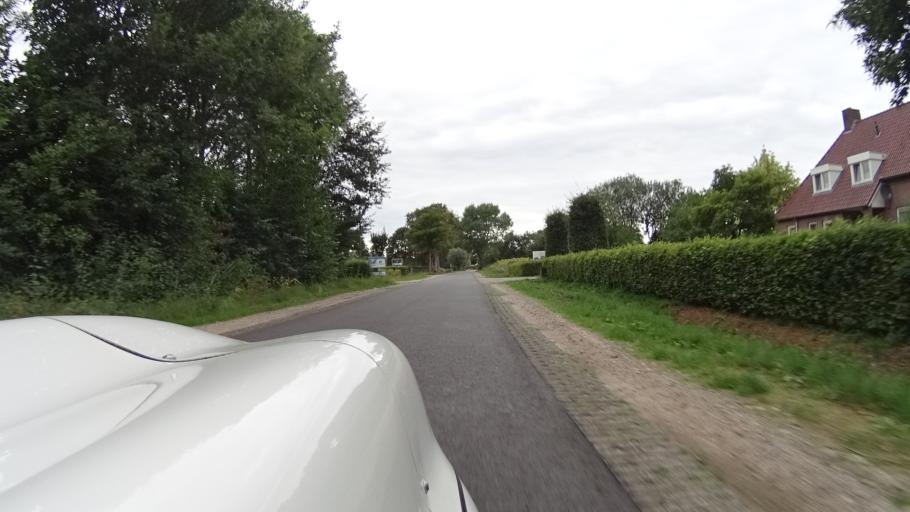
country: NL
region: North Brabant
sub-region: Gemeente Veghel
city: Mariaheide
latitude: 51.6536
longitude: 5.5674
